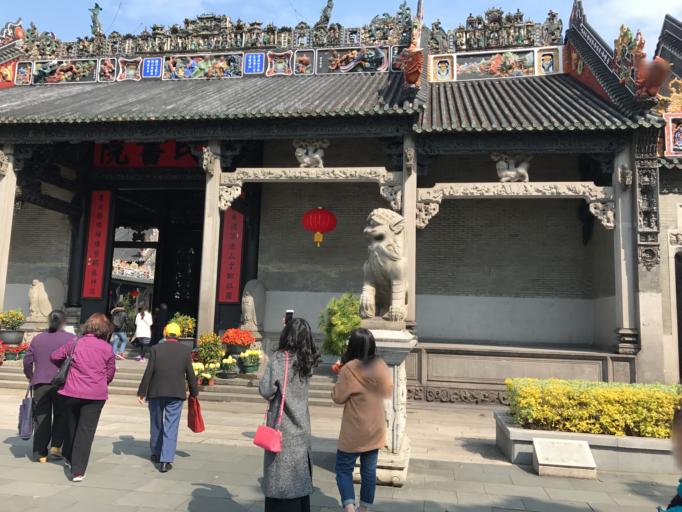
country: CN
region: Guangdong
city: Guangzhou
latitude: 23.1293
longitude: 113.2402
